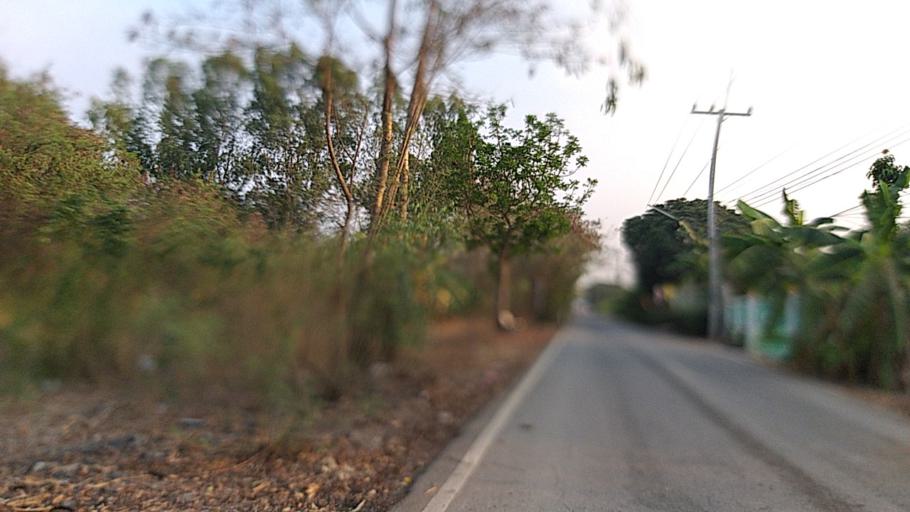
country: TH
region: Pathum Thani
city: Nong Suea
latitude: 14.0591
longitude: 100.8313
